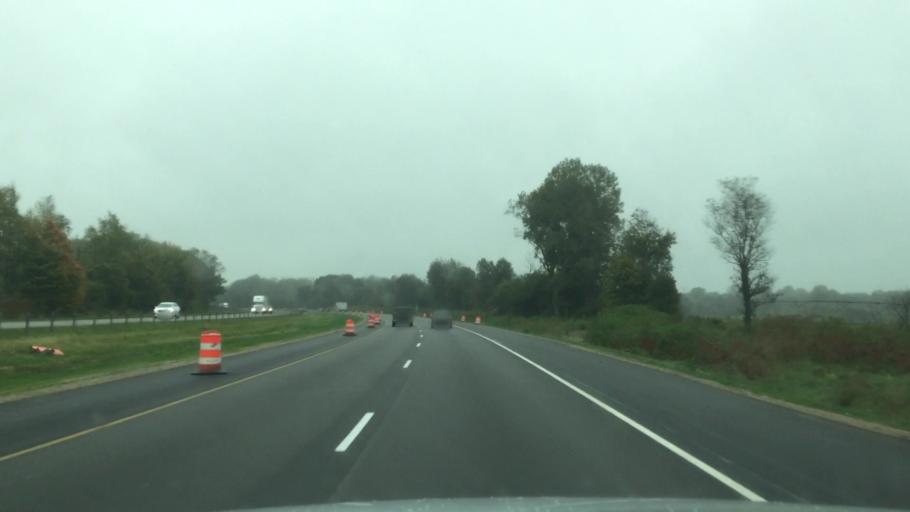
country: US
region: Michigan
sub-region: Van Buren County
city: Decatur
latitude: 42.1902
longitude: -86.0078
